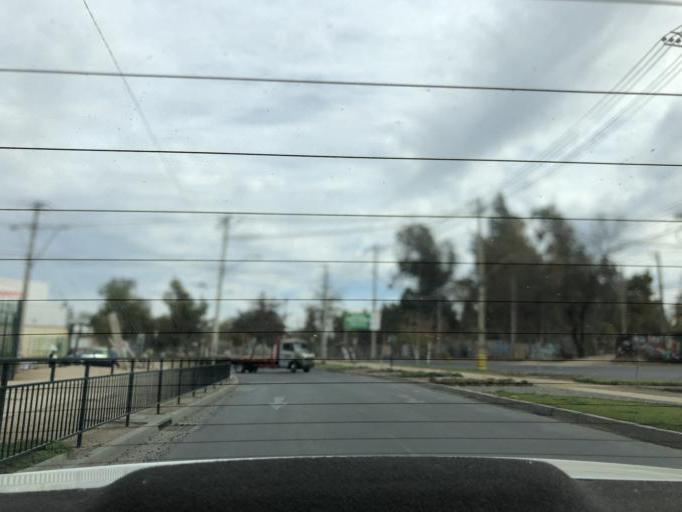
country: CL
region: Santiago Metropolitan
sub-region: Provincia de Cordillera
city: Puente Alto
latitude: -33.6101
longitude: -70.5505
